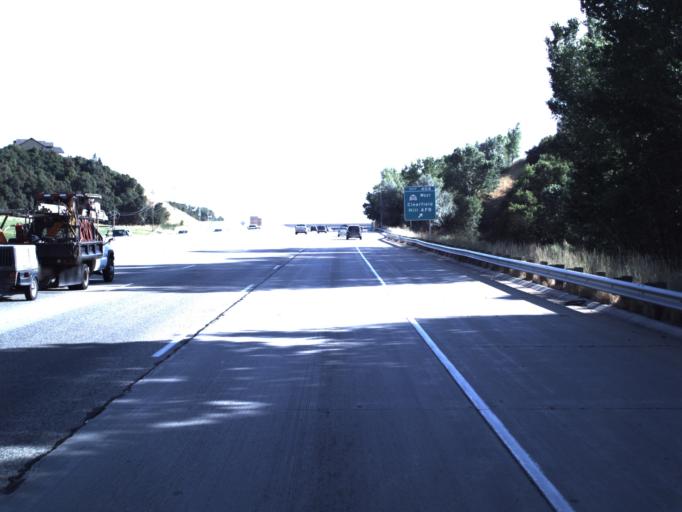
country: US
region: Utah
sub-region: Davis County
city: South Weber
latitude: 41.1126
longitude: -111.9093
